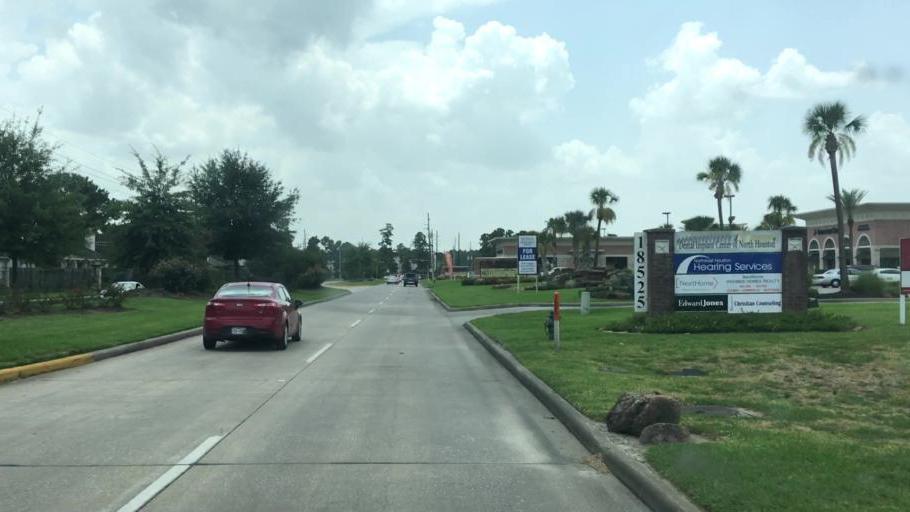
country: US
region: Texas
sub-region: Harris County
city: Atascocita
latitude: 29.9874
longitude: -95.1617
